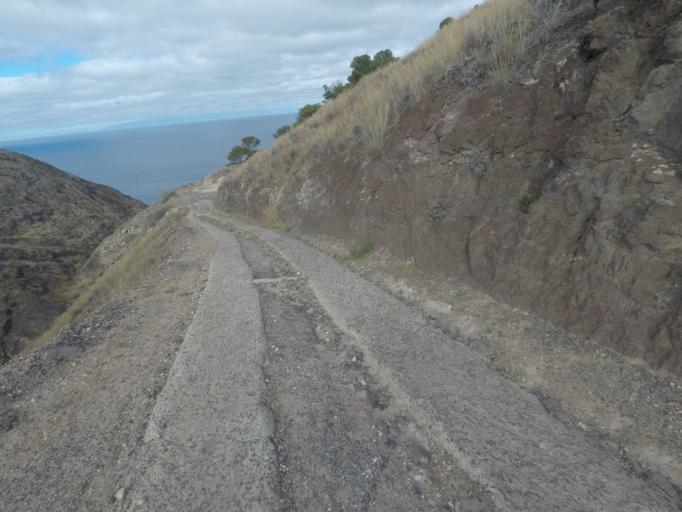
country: PT
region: Madeira
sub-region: Porto Santo
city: Vila de Porto Santo
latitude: 33.0324
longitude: -16.3855
